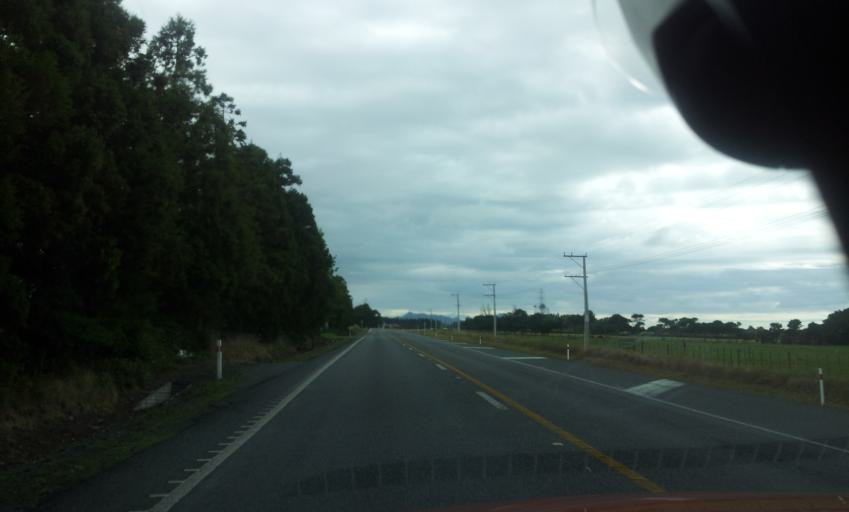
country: NZ
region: Northland
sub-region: Whangarei
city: Ruakaka
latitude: -35.9961
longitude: 174.4191
